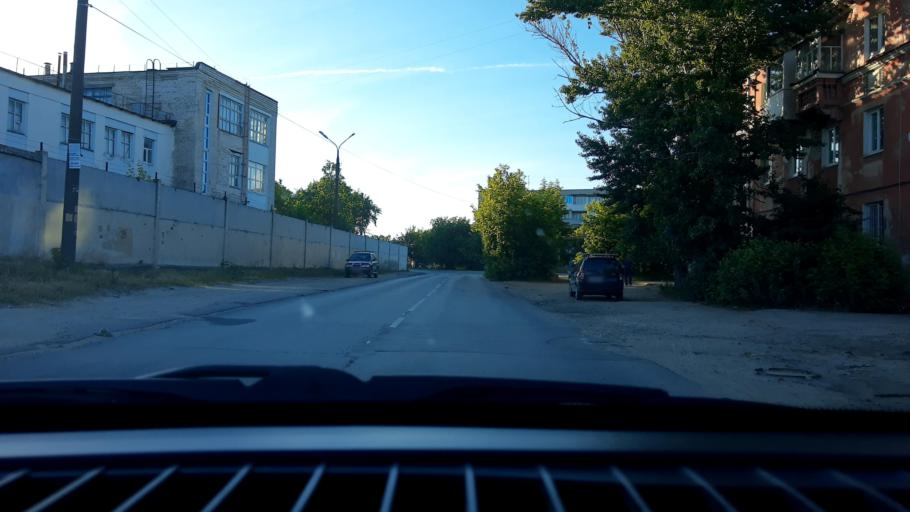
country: RU
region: Nizjnij Novgorod
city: Dzerzhinsk
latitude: 56.2390
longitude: 43.4898
